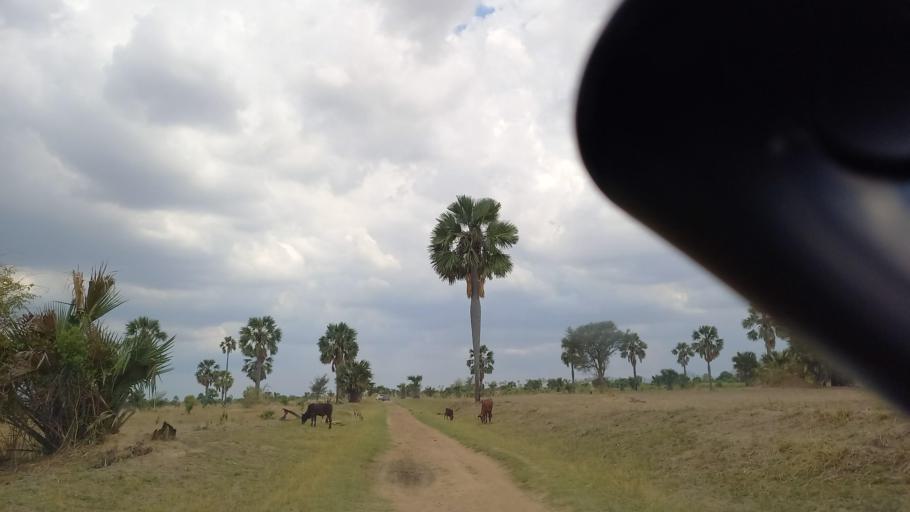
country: ZM
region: Lusaka
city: Kafue
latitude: -15.8278
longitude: 28.0561
